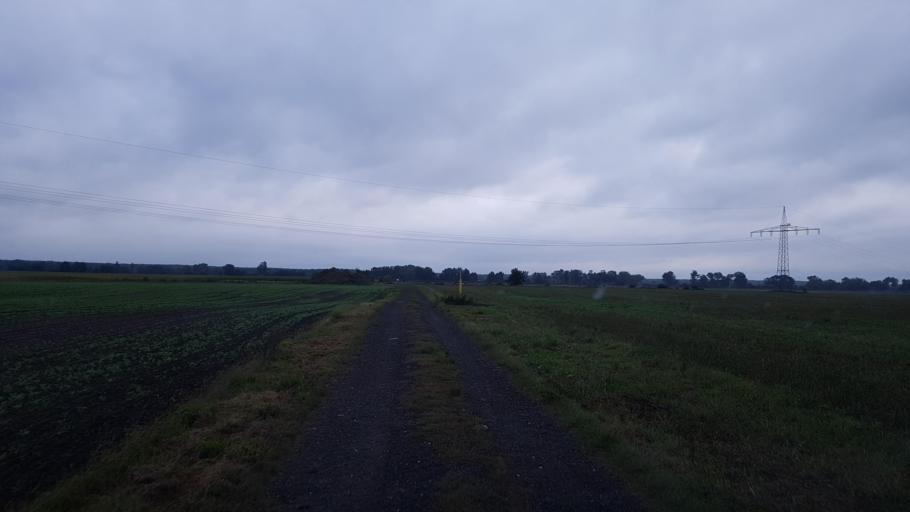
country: DE
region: Brandenburg
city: Plessa
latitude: 51.4545
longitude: 13.6518
